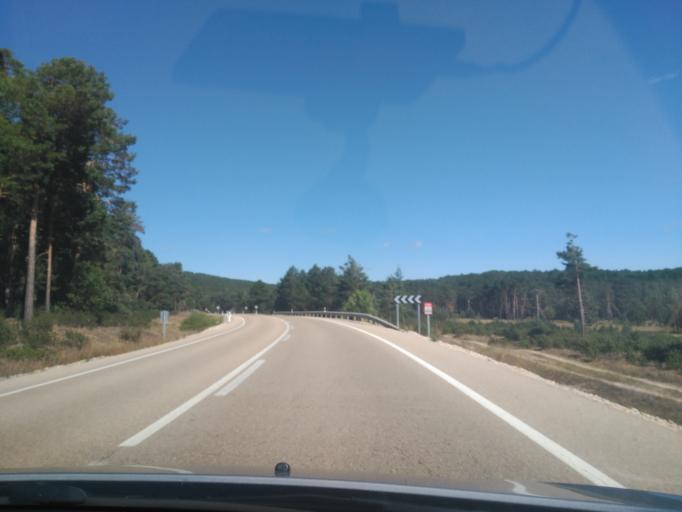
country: ES
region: Castille and Leon
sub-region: Provincia de Soria
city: Navaleno
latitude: 41.8371
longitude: -3.0338
